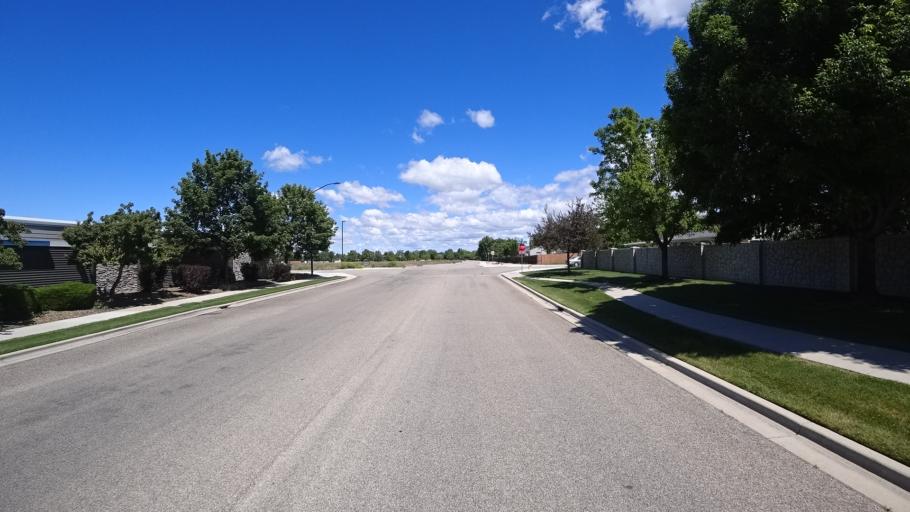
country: US
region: Idaho
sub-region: Ada County
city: Meridian
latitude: 43.6371
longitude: -116.3497
